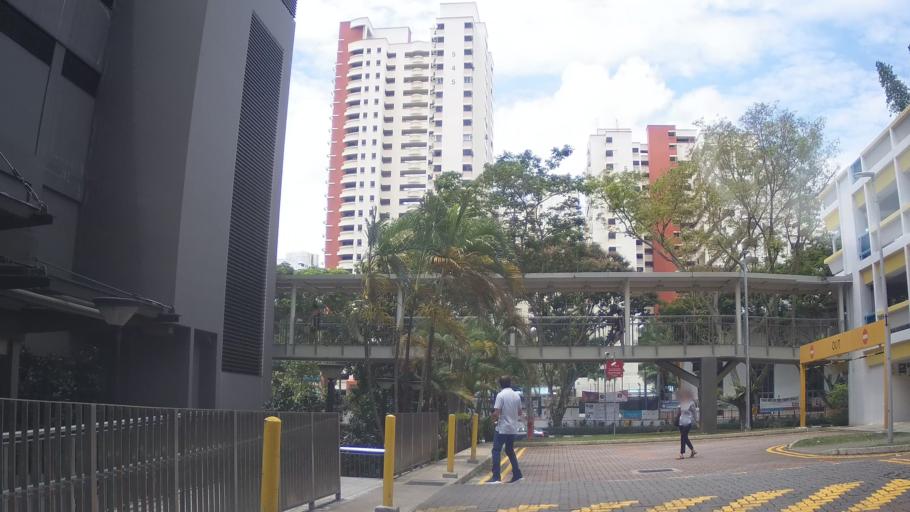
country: MY
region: Johor
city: Johor Bahru
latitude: 1.3805
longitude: 103.7644
